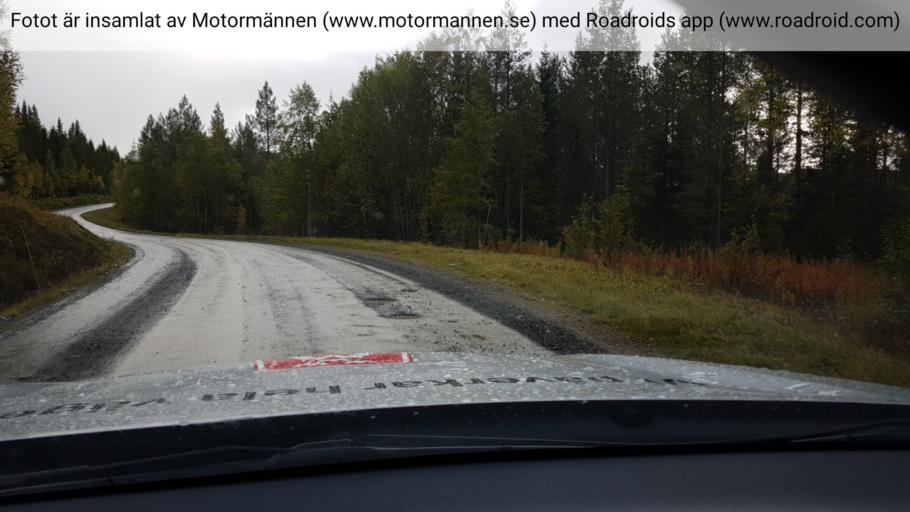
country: SE
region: Jaemtland
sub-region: Krokoms Kommun
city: Valla
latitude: 64.1059
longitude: 14.1501
